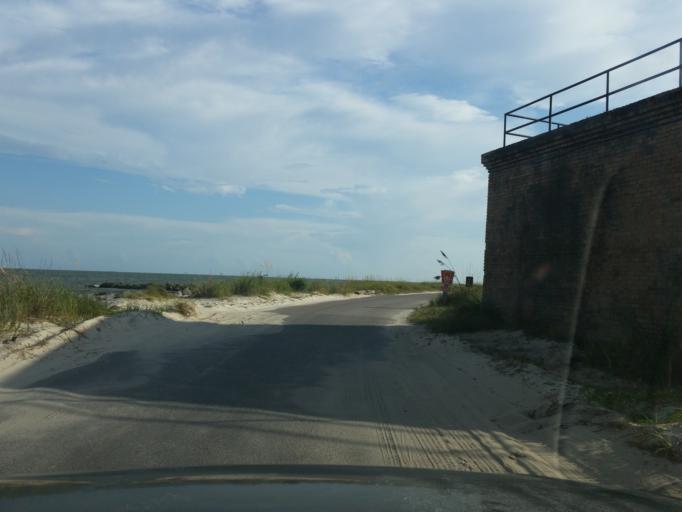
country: US
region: Alabama
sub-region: Mobile County
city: Dauphin Island
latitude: 30.2482
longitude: -88.0748
